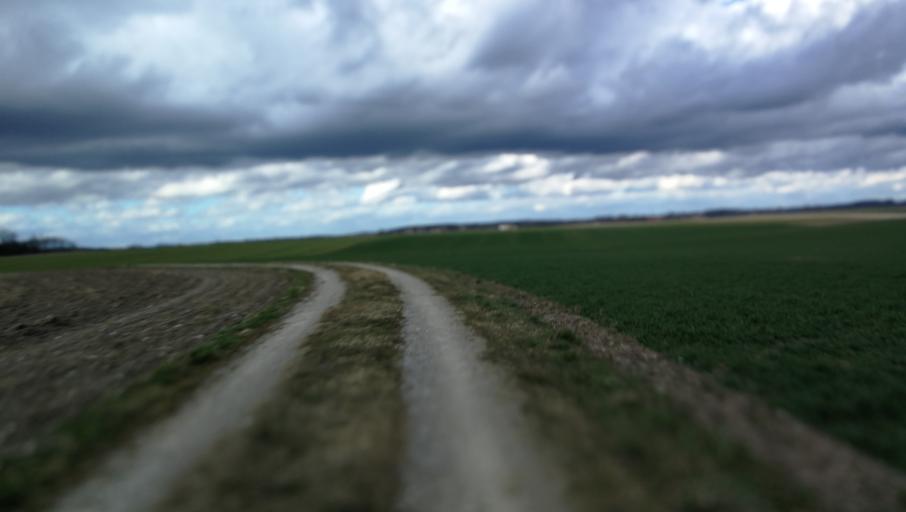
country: DE
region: Bavaria
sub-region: Upper Bavaria
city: Fuerstenfeldbruck
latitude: 48.1939
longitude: 11.2127
